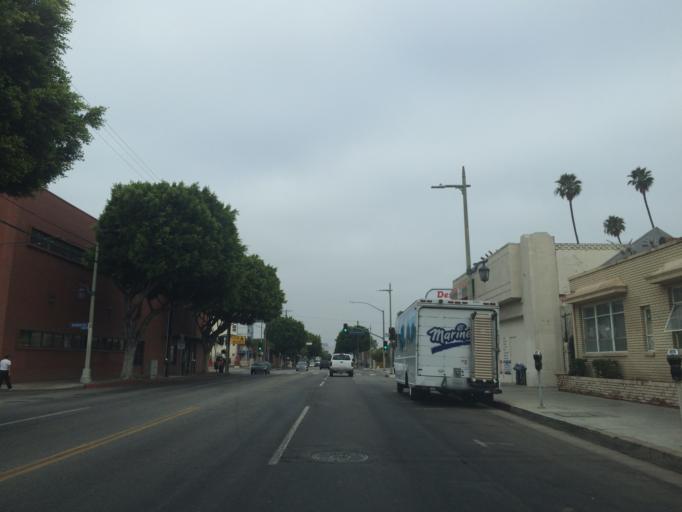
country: US
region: California
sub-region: Los Angeles County
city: Echo Park
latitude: 34.0473
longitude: -118.2882
